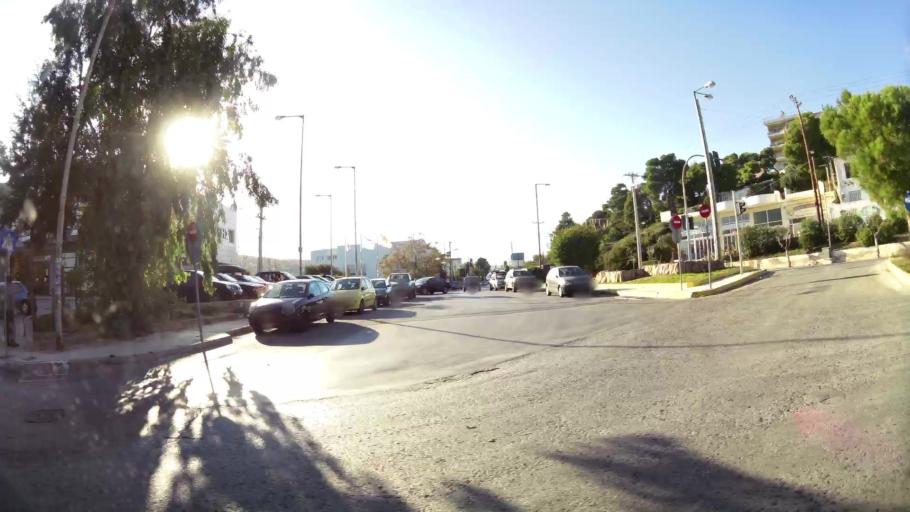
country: GR
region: Attica
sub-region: Nomarchia Anatolikis Attikis
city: Rafina
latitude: 38.0187
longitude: 24.0037
